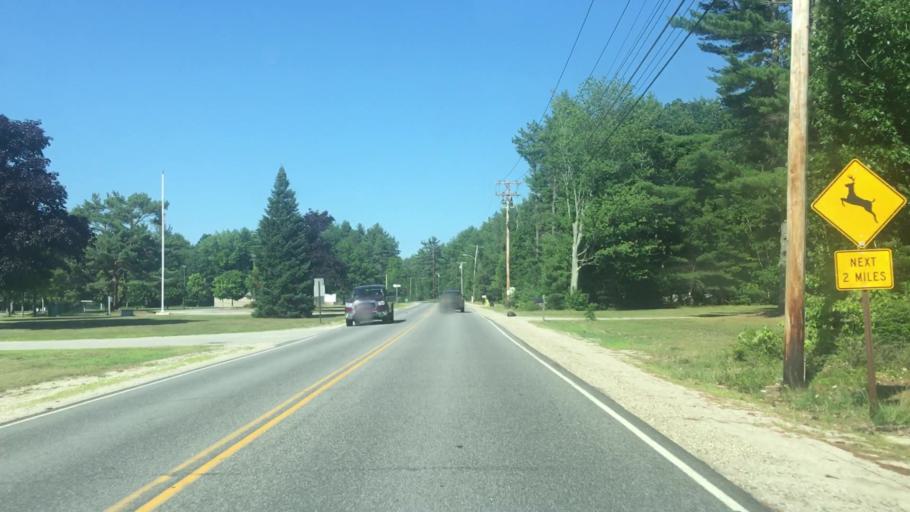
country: US
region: Maine
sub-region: York County
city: Hollis Center
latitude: 43.6939
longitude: -70.5961
